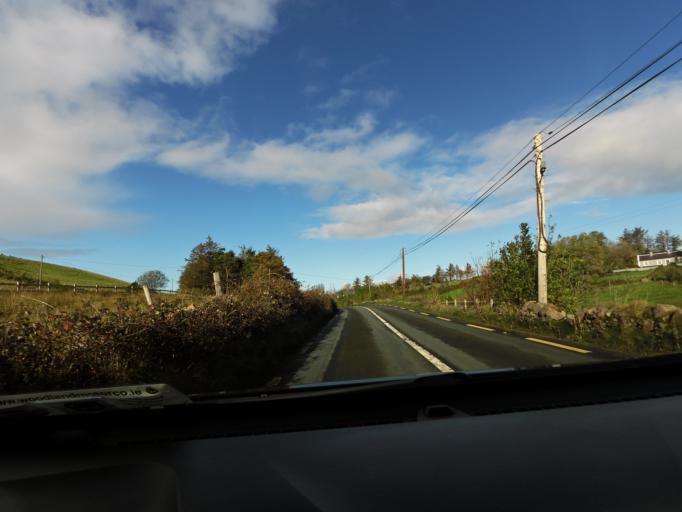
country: IE
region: Connaught
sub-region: Maigh Eo
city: Westport
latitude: 53.8216
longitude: -9.5356
